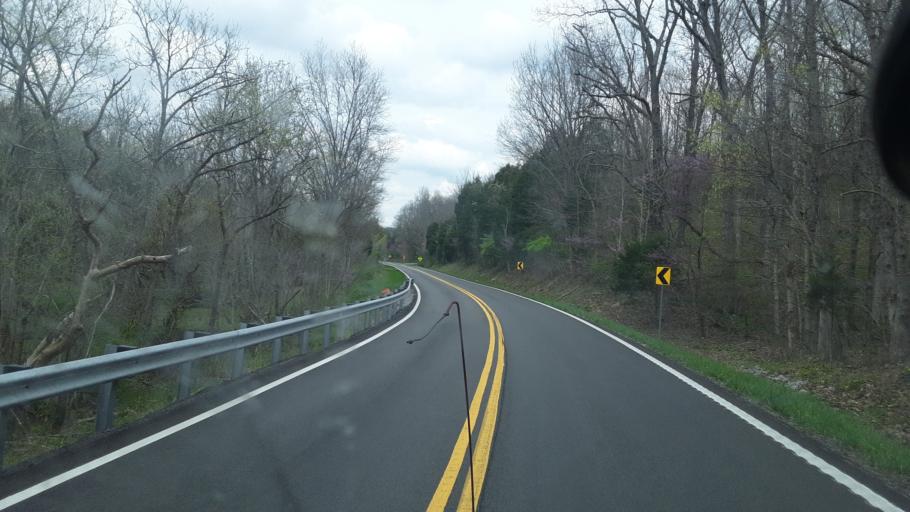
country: US
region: Kentucky
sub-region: Grant County
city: Dry Ridge
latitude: 38.6541
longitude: -84.6776
